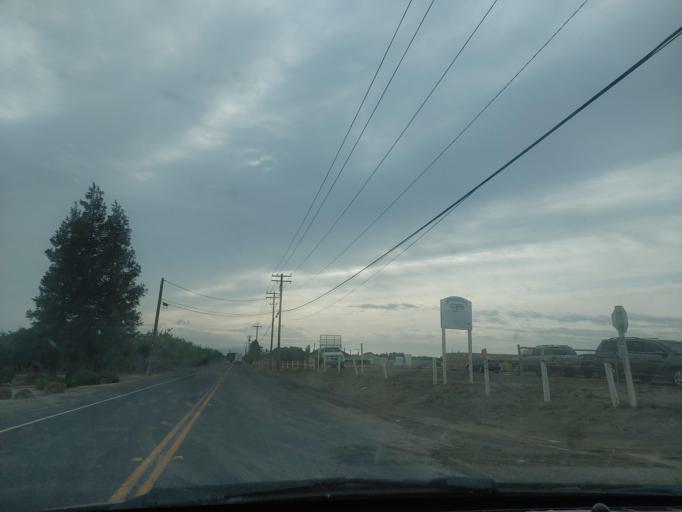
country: US
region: California
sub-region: Stanislaus County
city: Salida
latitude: 37.6817
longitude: -121.1104
